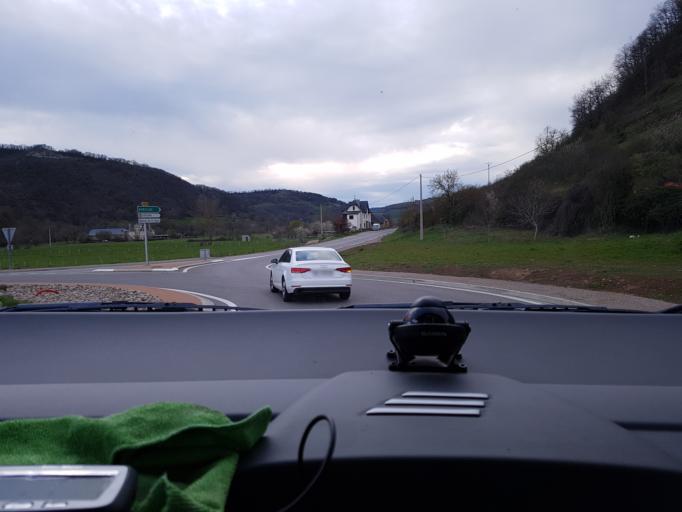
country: FR
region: Midi-Pyrenees
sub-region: Departement de l'Aveyron
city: Espalion
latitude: 44.5320
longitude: 2.7382
